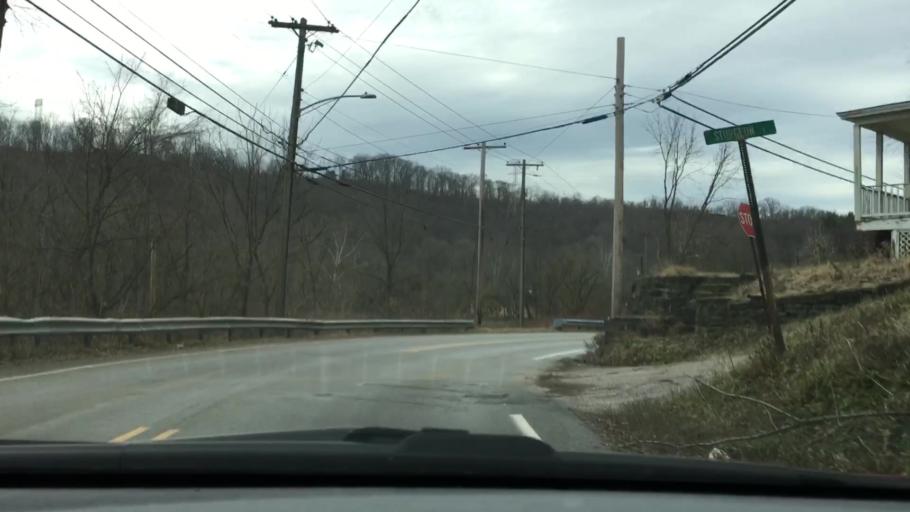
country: US
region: Pennsylvania
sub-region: Allegheny County
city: Sturgeon
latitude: 40.3780
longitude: -80.2168
